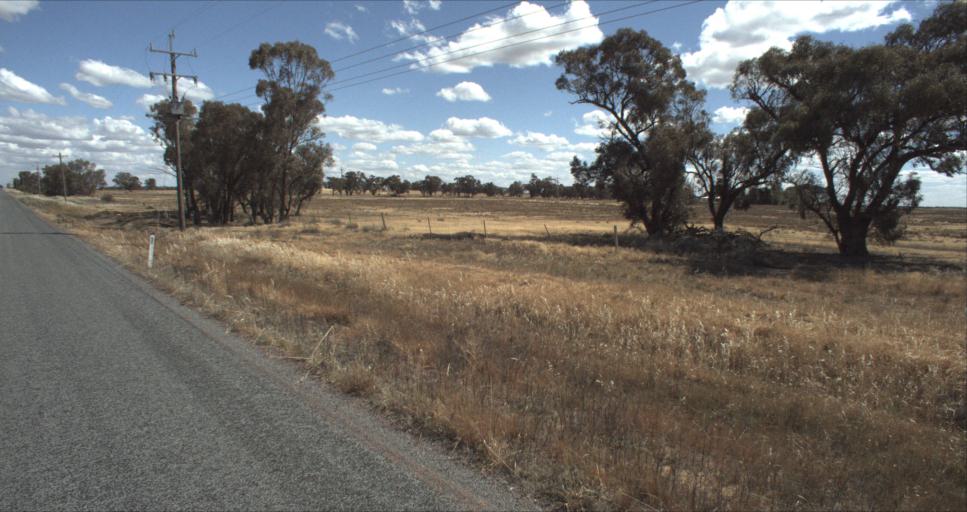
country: AU
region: New South Wales
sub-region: Leeton
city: Leeton
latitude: -34.4855
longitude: 146.2483
